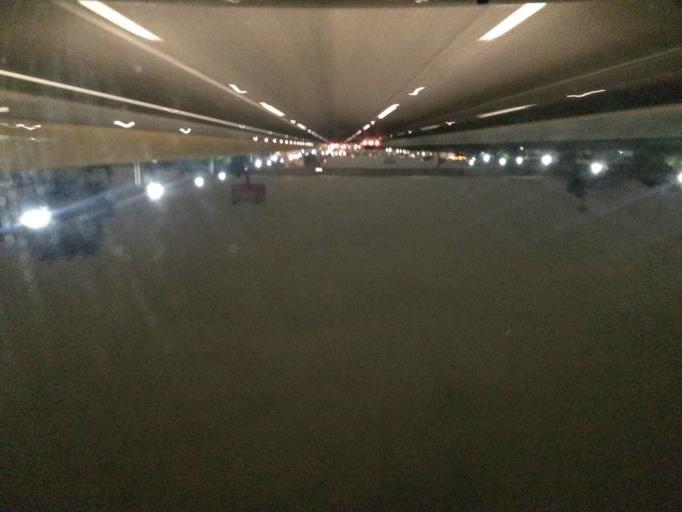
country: MX
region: Mexico
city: San Miguel Xico Viejo
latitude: 19.3051
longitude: -98.9363
